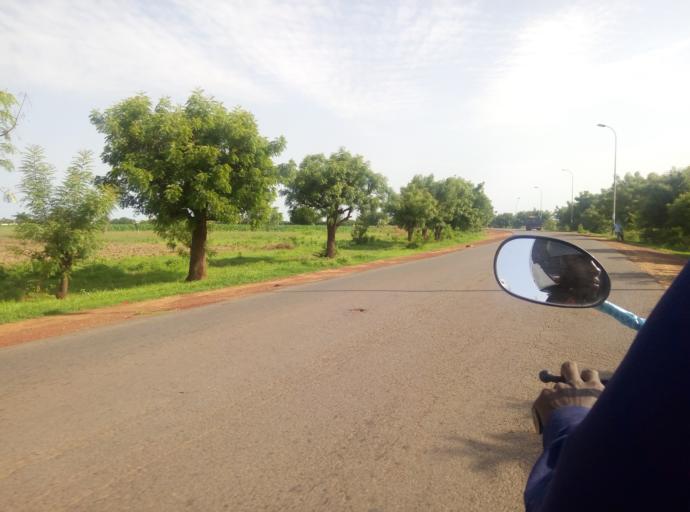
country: ML
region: Bamako
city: Bamako
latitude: 12.5505
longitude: -7.9505
